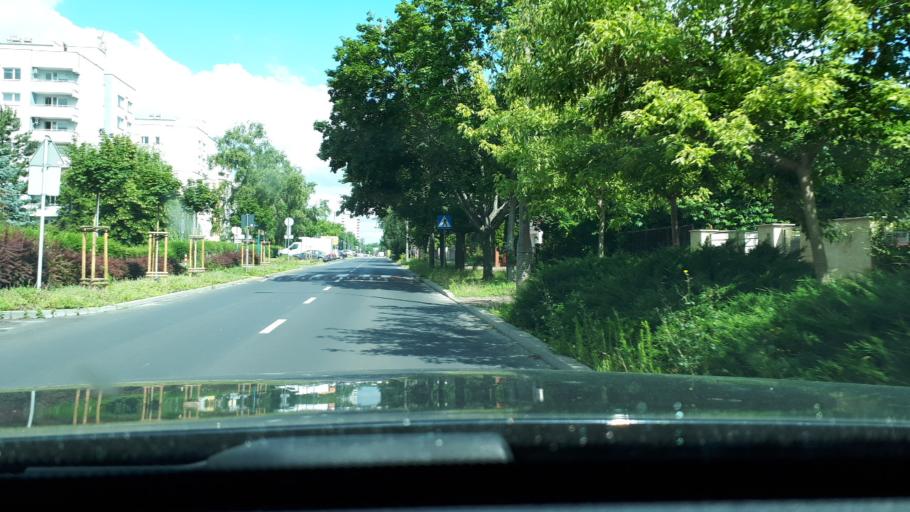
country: PL
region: Masovian Voivodeship
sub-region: Warszawa
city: Wilanow
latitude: 52.1702
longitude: 21.0759
